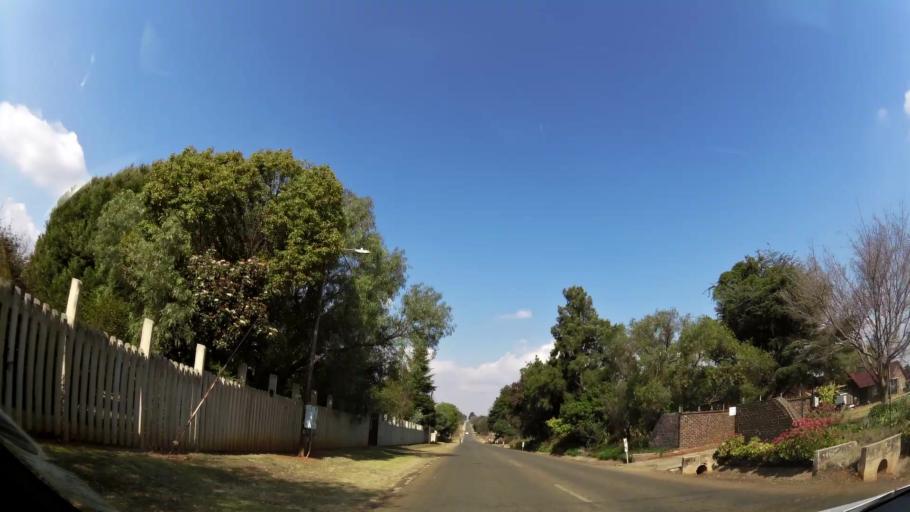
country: ZA
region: Mpumalanga
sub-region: Nkangala District Municipality
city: Delmas
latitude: -26.1773
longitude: 28.5374
